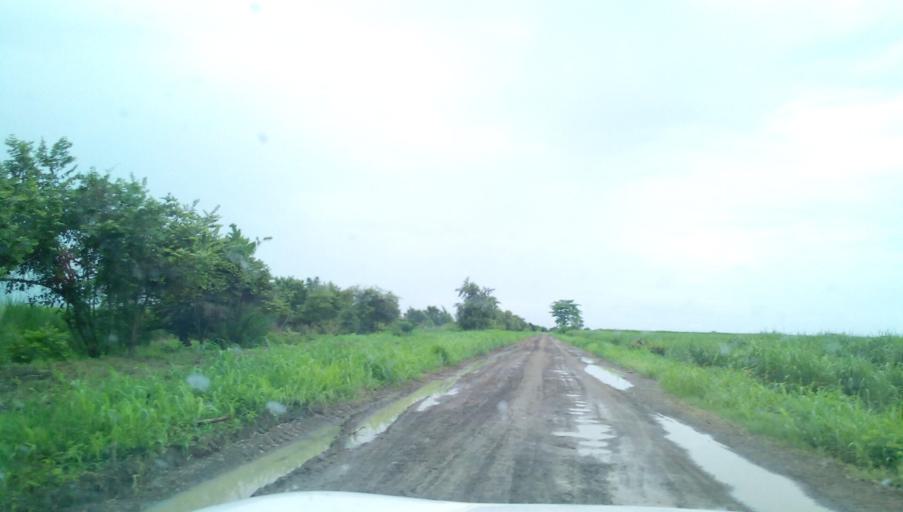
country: MX
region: Veracruz
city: Panuco
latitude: 21.8365
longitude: -98.1104
